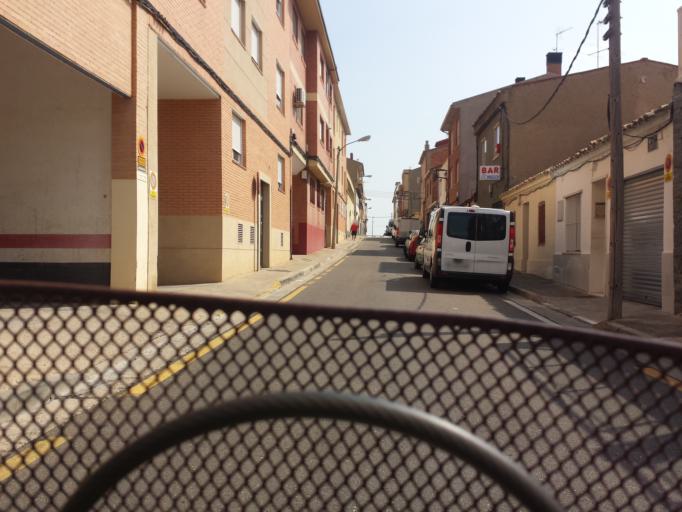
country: ES
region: Aragon
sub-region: Provincia de Zaragoza
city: Oliver-Valdefierro, Oliver, Valdefierro
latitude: 41.6369
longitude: -0.9330
